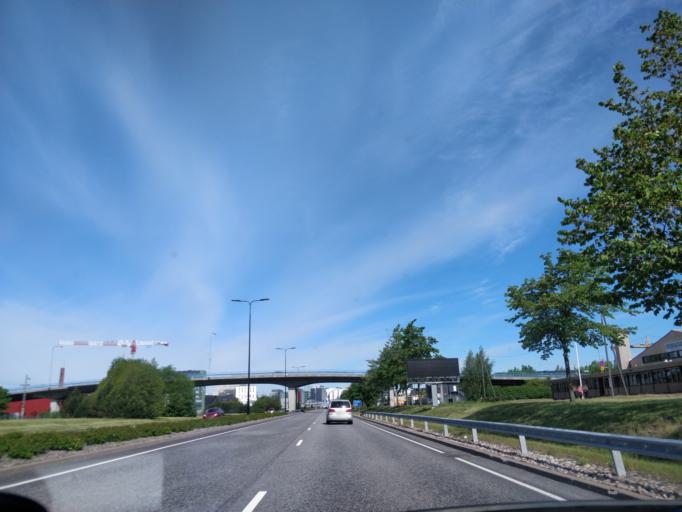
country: FI
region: Varsinais-Suomi
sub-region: Turku
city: Turku
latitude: 60.4440
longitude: 22.3094
